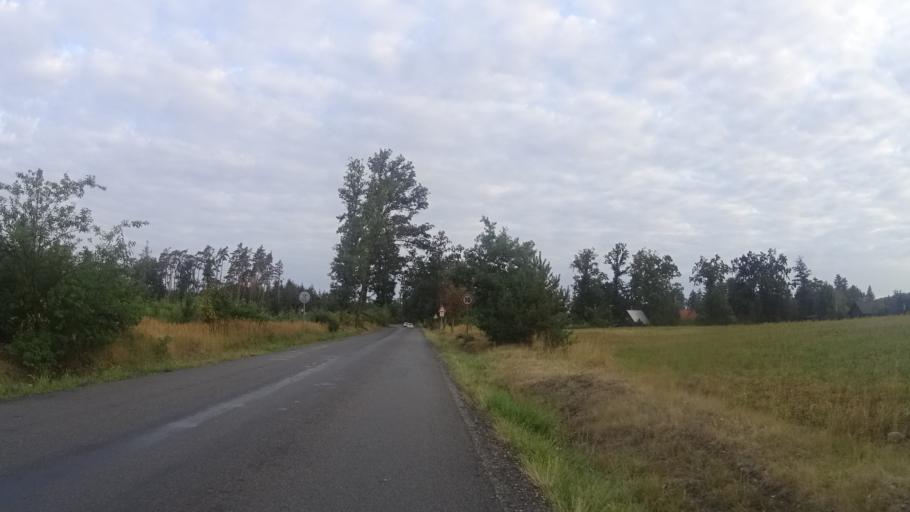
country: CZ
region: Kralovehradecky
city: Cernilov
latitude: 50.2033
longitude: 15.9294
